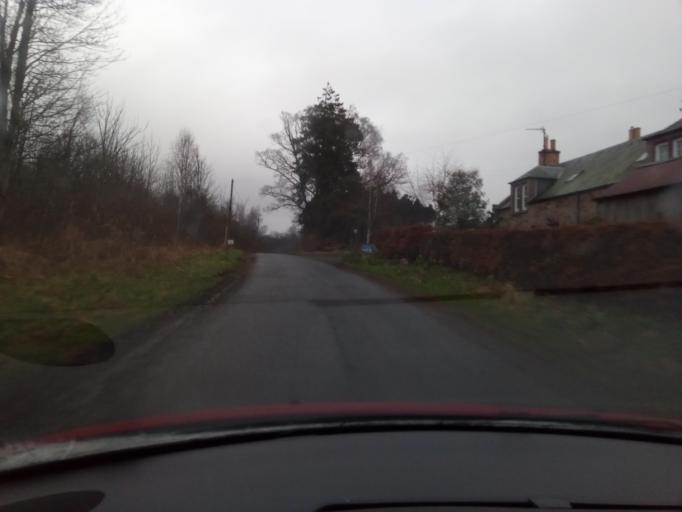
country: GB
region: Scotland
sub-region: The Scottish Borders
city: Kelso
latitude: 55.5517
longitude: -2.4314
